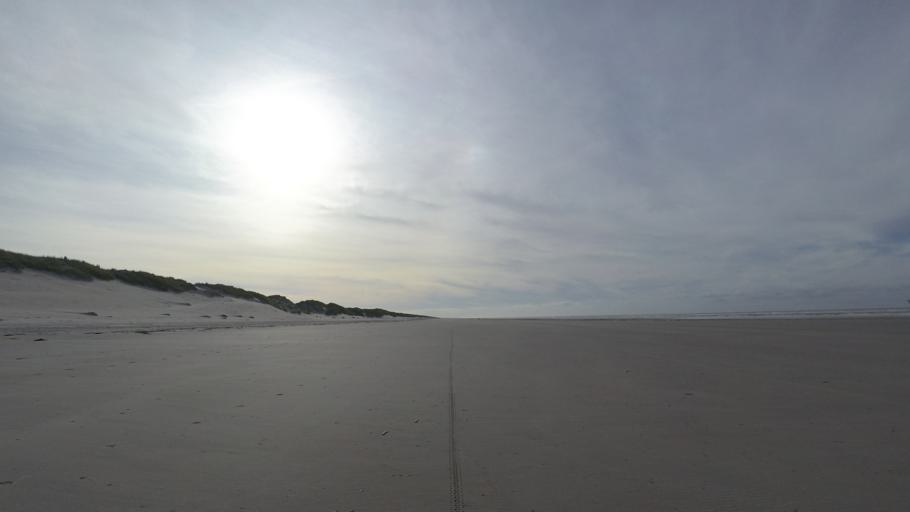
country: NL
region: Friesland
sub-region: Gemeente Dongeradeel
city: Holwerd
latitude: 53.4670
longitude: 5.8937
